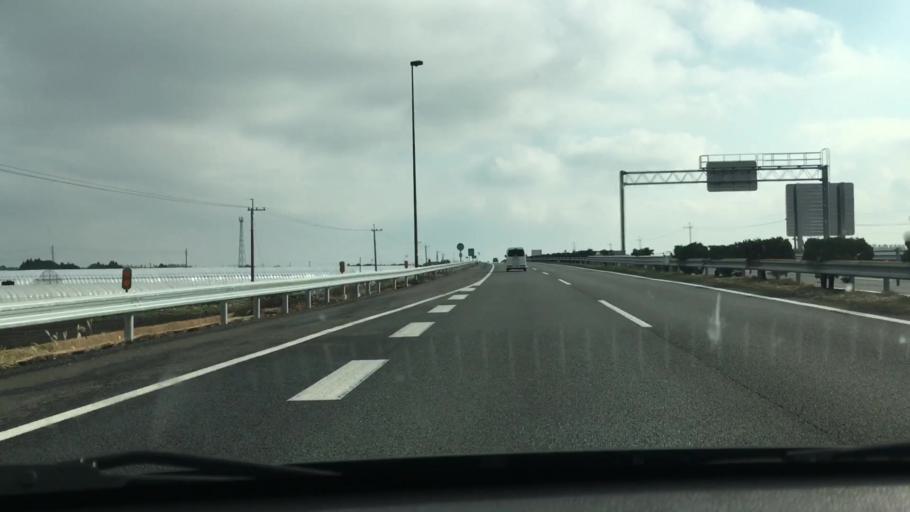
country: JP
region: Kumamoto
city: Ueki
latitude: 32.8917
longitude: 130.7207
